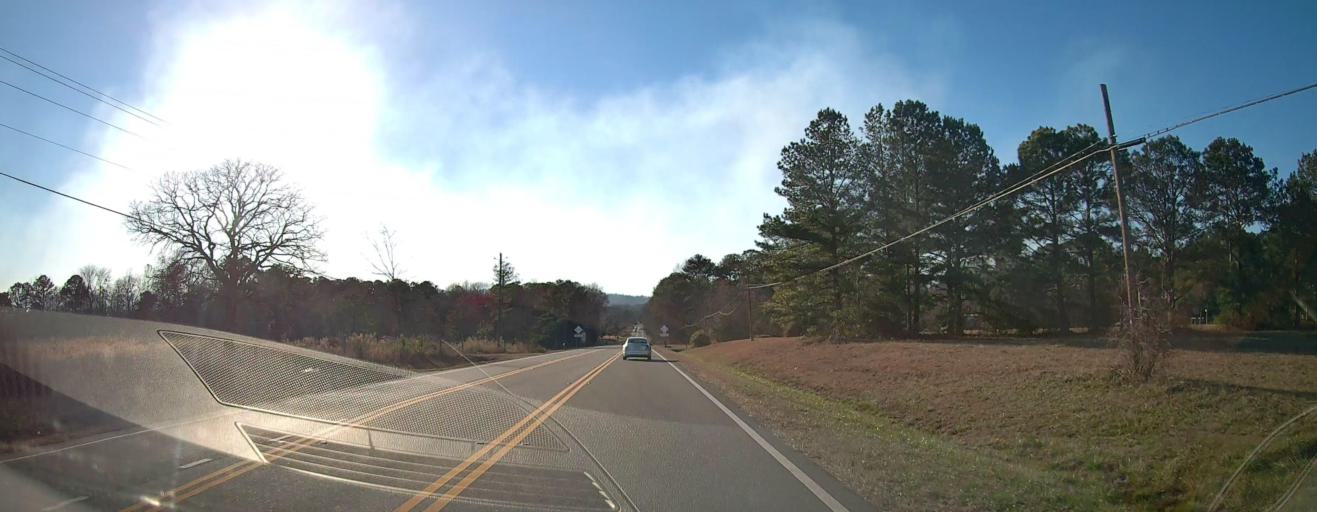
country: US
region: Georgia
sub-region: Meriwether County
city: Manchester
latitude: 32.8772
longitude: -84.6454
